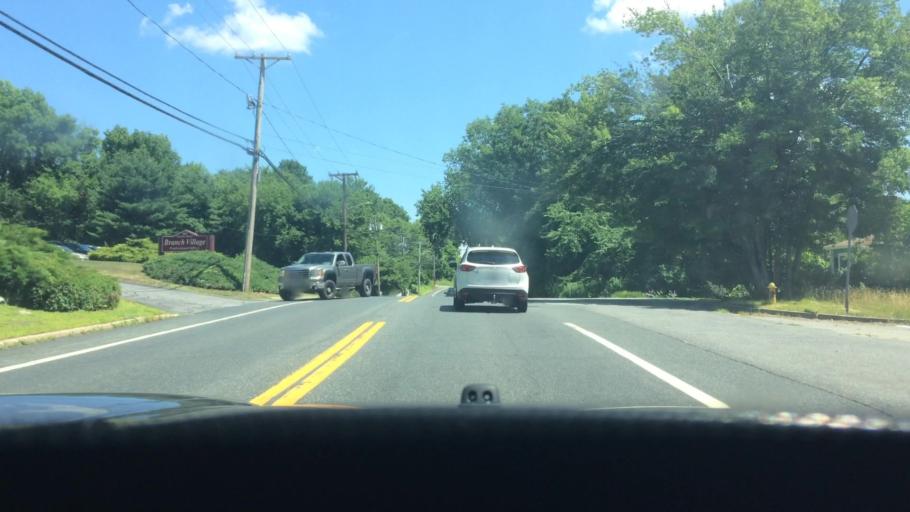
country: US
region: Massachusetts
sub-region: Worcester County
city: Blackstone
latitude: 41.9976
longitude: -71.5467
